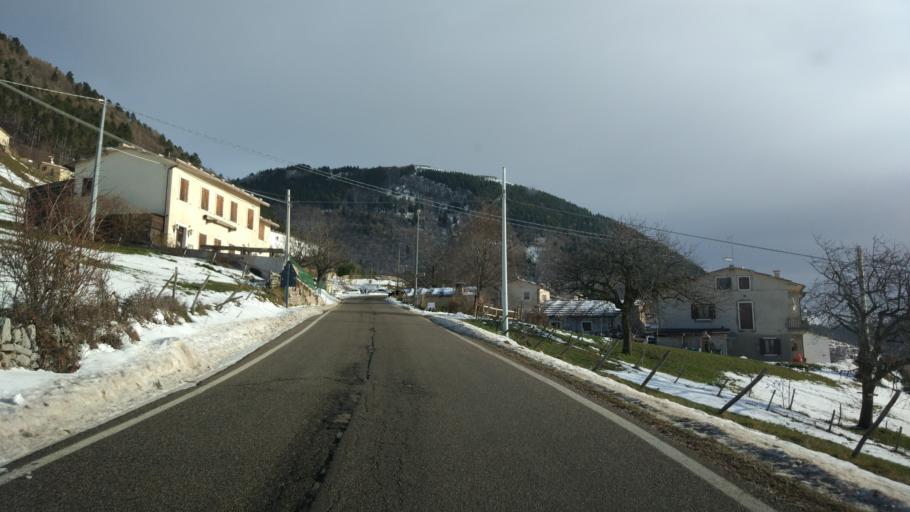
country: IT
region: Veneto
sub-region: Provincia di Verona
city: Sant'Anna d'Alfaedo
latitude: 45.6638
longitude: 10.9424
